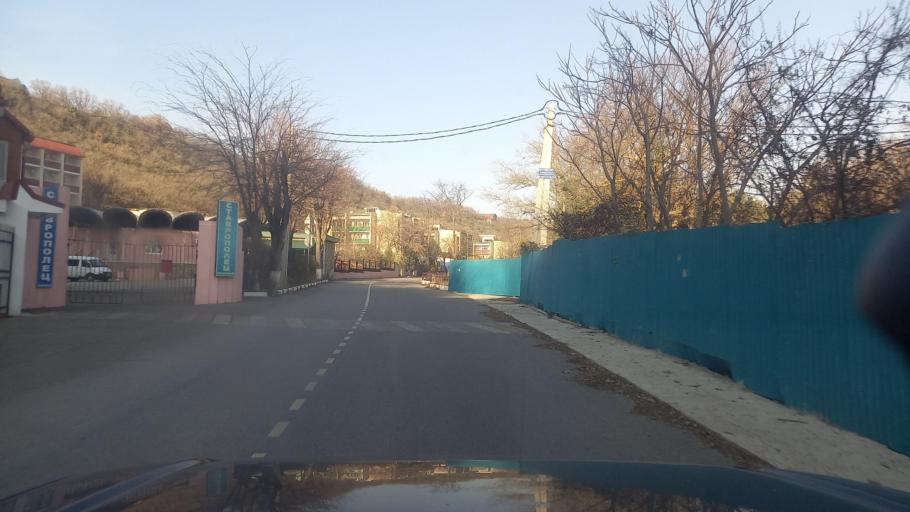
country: RU
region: Krasnodarskiy
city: Myskhako
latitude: 44.6604
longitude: 37.6848
